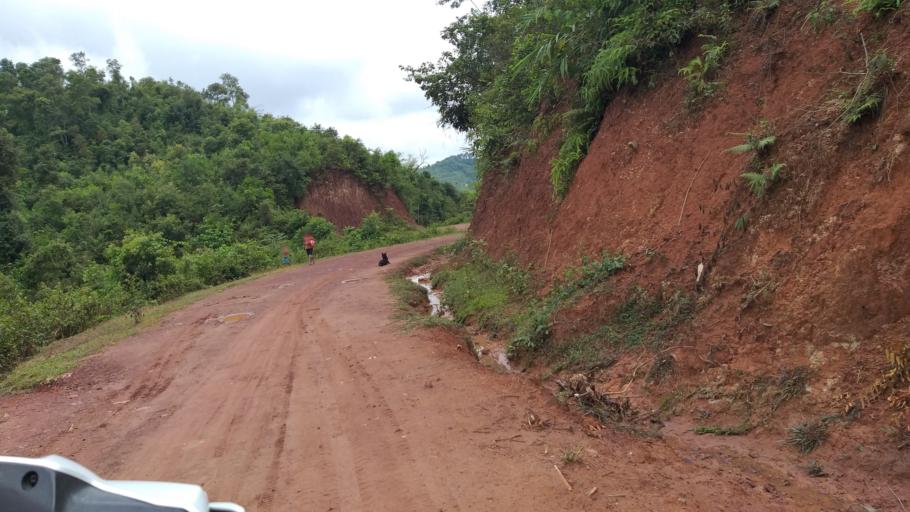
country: LA
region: Phongsali
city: Khoa
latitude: 21.3860
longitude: 102.6349
